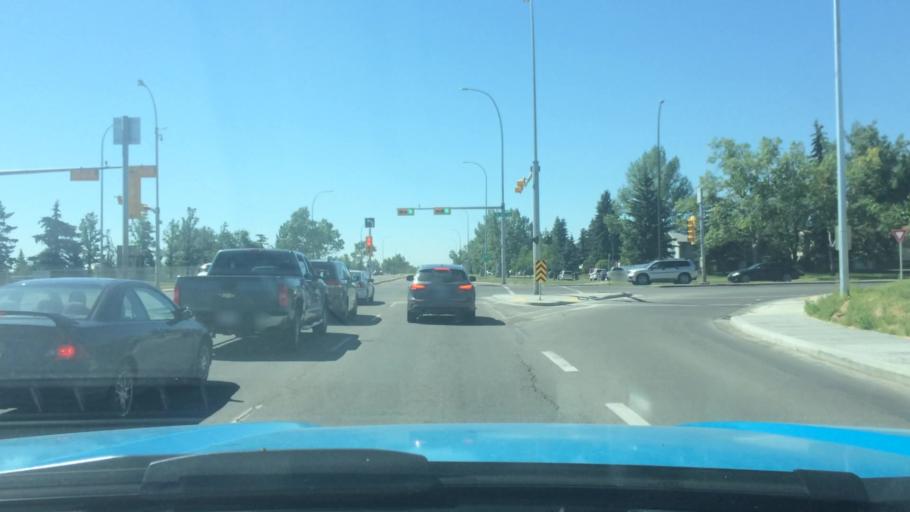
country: CA
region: Alberta
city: Calgary
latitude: 51.0820
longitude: -113.9584
